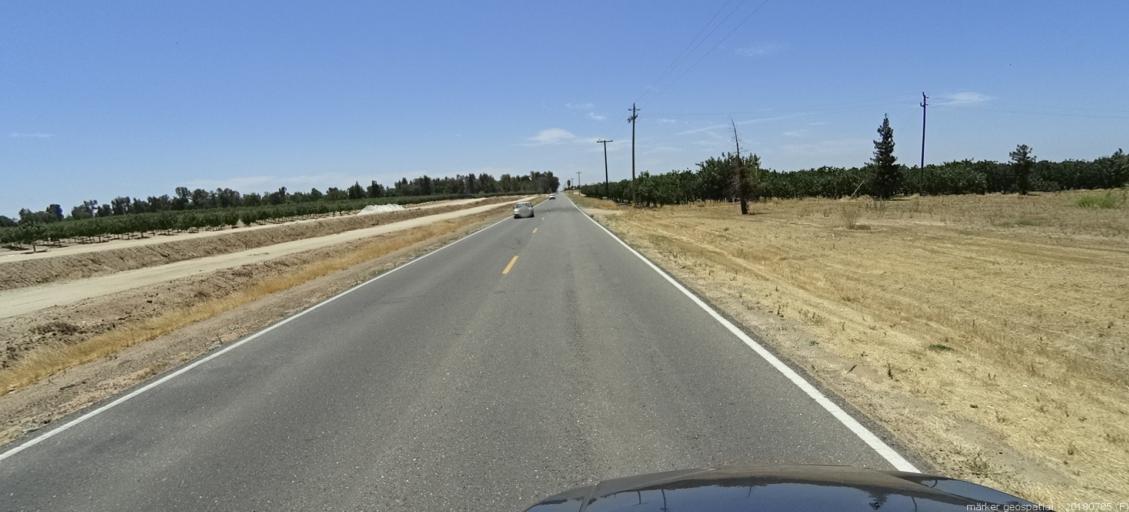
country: US
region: California
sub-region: Madera County
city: Madera Acres
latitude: 37.0368
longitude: -120.0744
